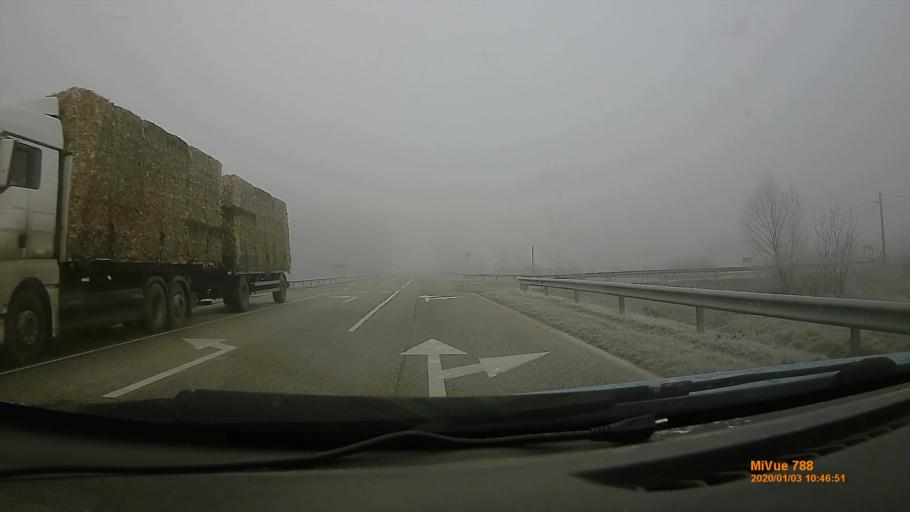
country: HU
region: Tolna
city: Bataszek
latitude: 46.2070
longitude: 18.7313
